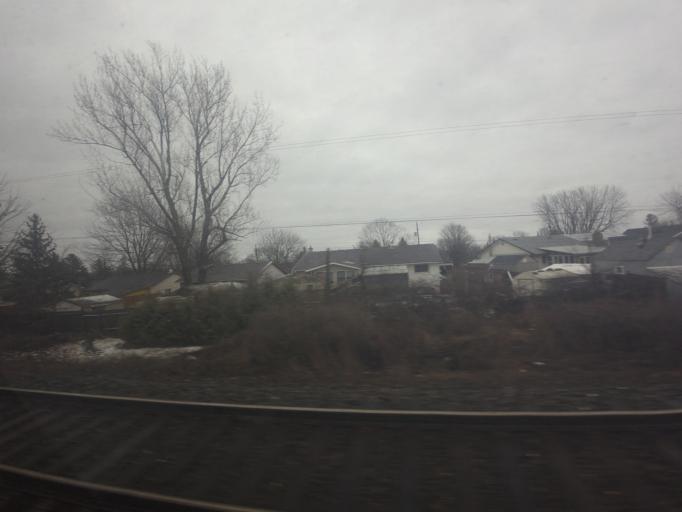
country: CA
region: Ontario
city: Kingston
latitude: 44.2279
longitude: -76.6380
